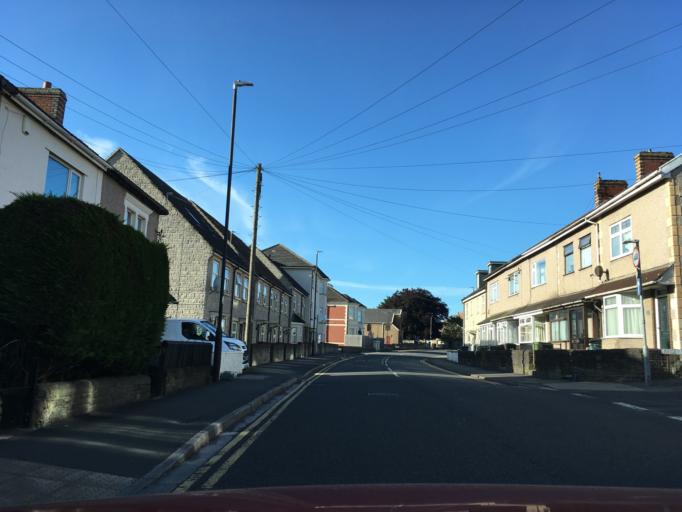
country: GB
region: England
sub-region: South Gloucestershire
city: Kingswood
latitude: 51.4604
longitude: -2.5053
